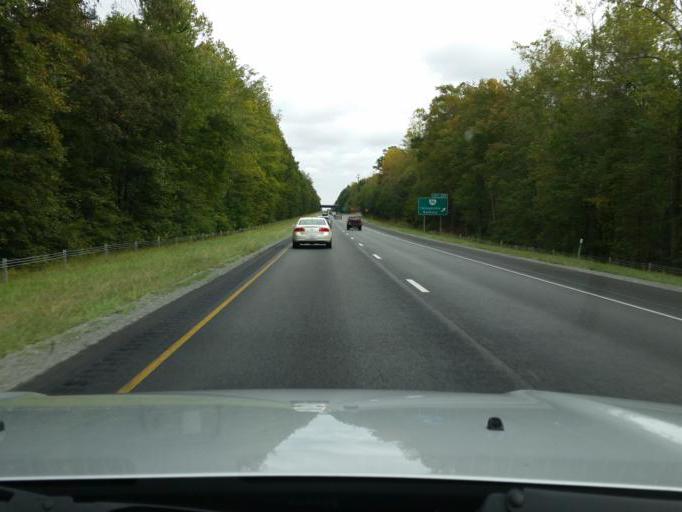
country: US
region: Virginia
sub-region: New Kent County
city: New Kent
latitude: 37.5057
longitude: -77.0946
